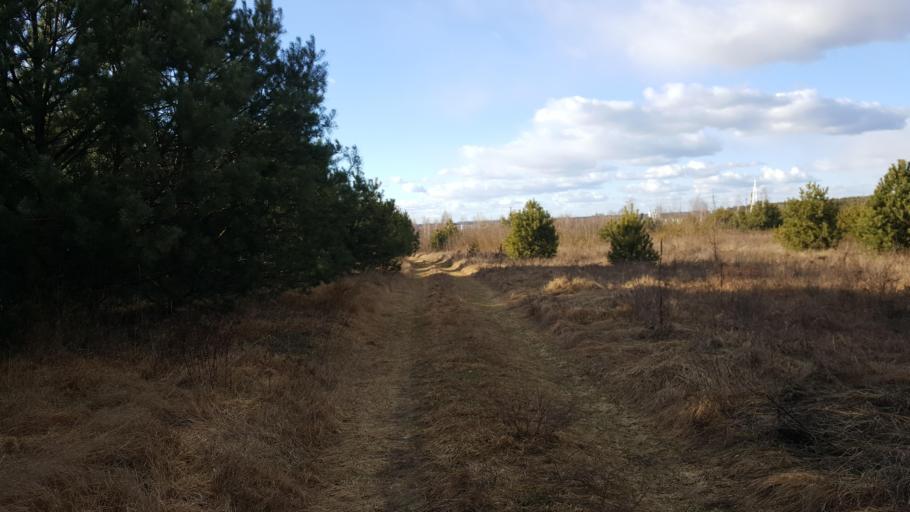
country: BY
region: Brest
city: Kamyanyets
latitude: 52.3860
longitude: 23.8401
